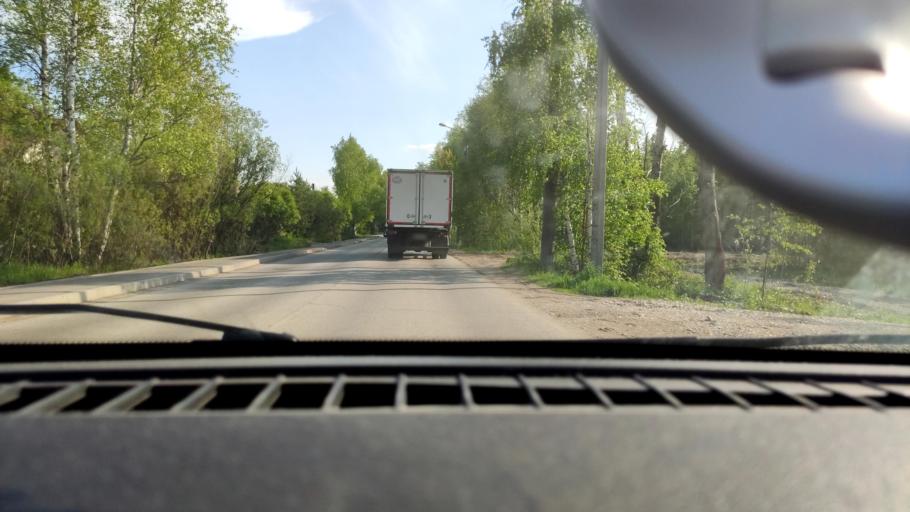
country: RU
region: Perm
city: Perm
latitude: 58.1544
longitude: 56.3043
